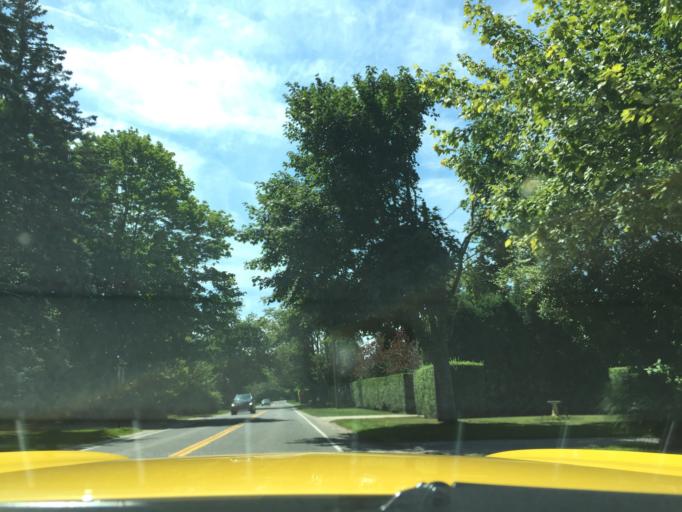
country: US
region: New York
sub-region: Suffolk County
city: Bridgehampton
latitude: 40.9340
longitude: -72.3096
